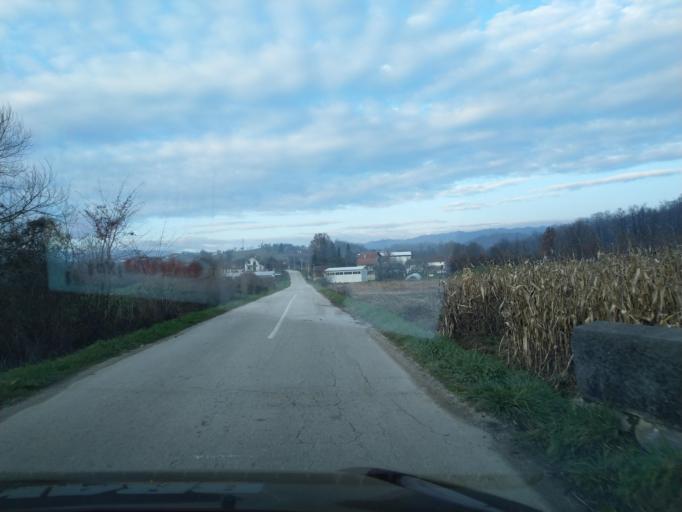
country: RS
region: Central Serbia
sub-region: Zlatiborski Okrug
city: Kosjeric
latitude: 43.9260
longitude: 19.8978
